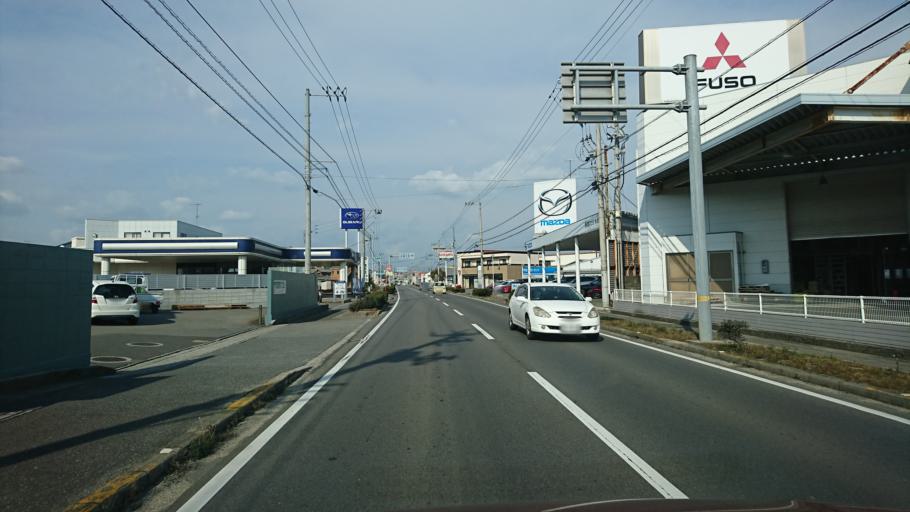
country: JP
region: Ehime
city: Saijo
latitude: 34.0136
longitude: 133.0387
